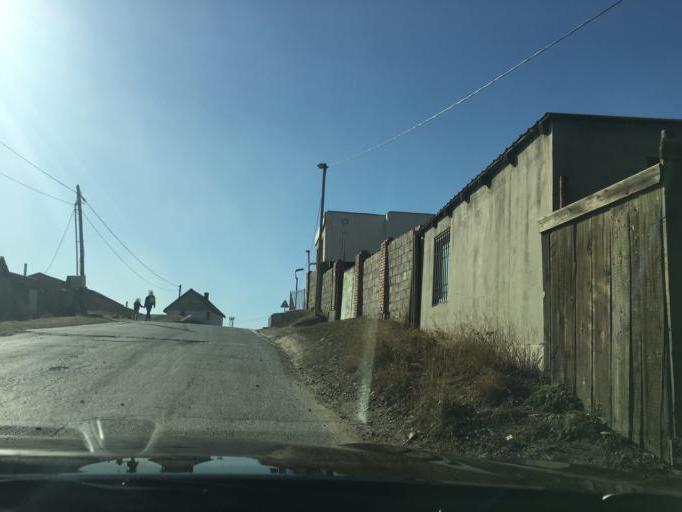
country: MN
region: Ulaanbaatar
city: Ulaanbaatar
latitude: 47.9316
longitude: 106.8789
